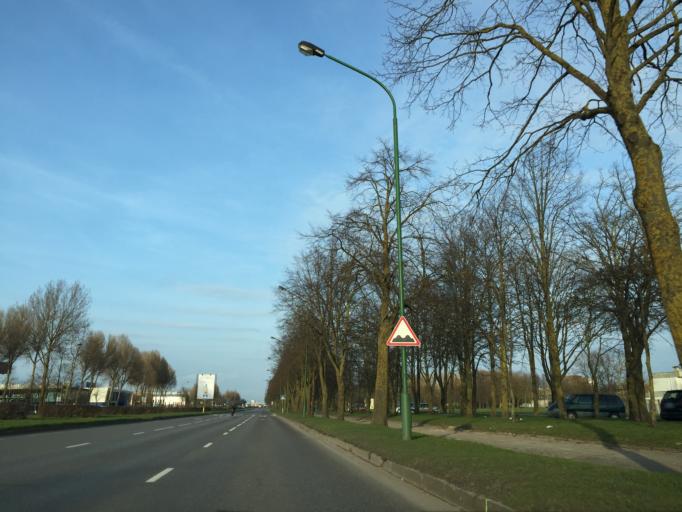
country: LT
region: Klaipedos apskritis
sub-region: Klaipeda
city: Klaipeda
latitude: 55.6884
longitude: 21.1656
